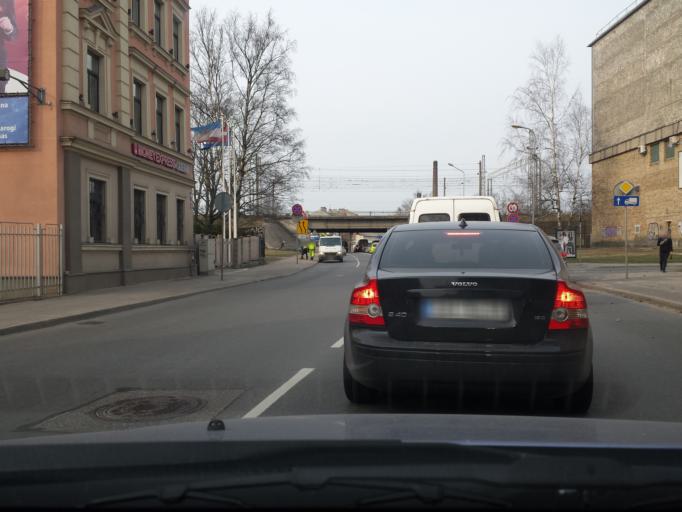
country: LV
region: Riga
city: Riga
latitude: 56.9456
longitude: 24.1336
